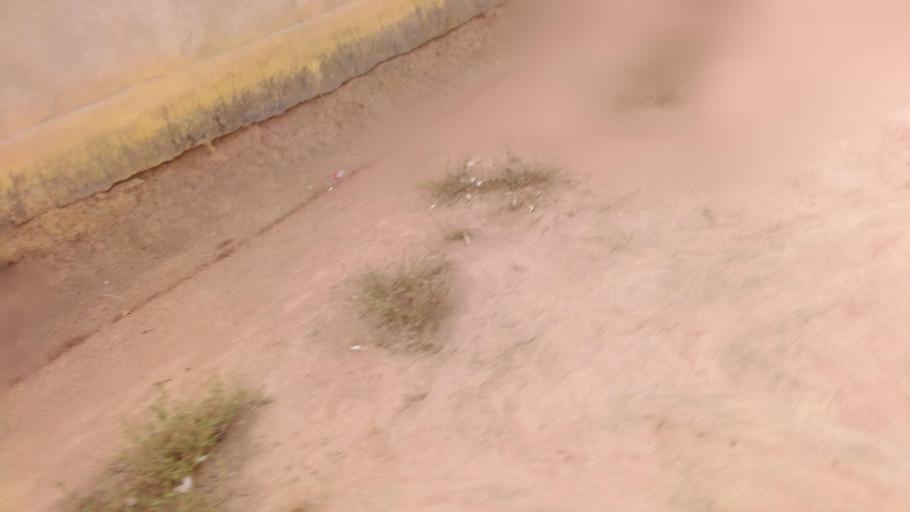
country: SL
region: Southern Province
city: Sumbuya
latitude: 7.6017
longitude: -12.1611
